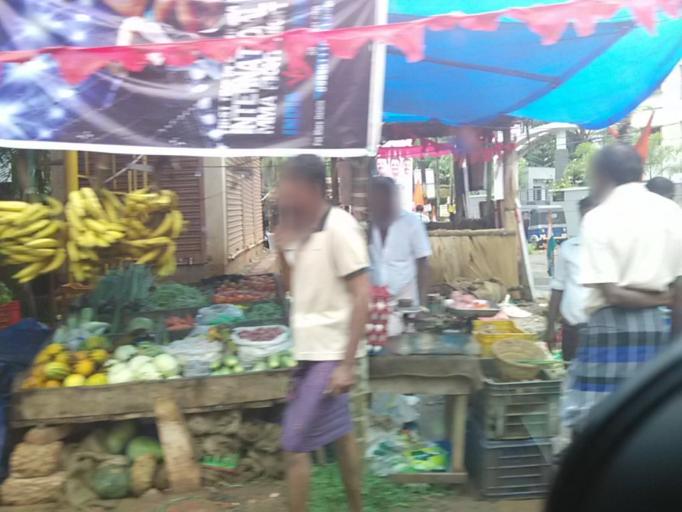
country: IN
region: Kerala
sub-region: Kozhikode
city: Kozhikode
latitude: 11.2781
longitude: 75.8095
